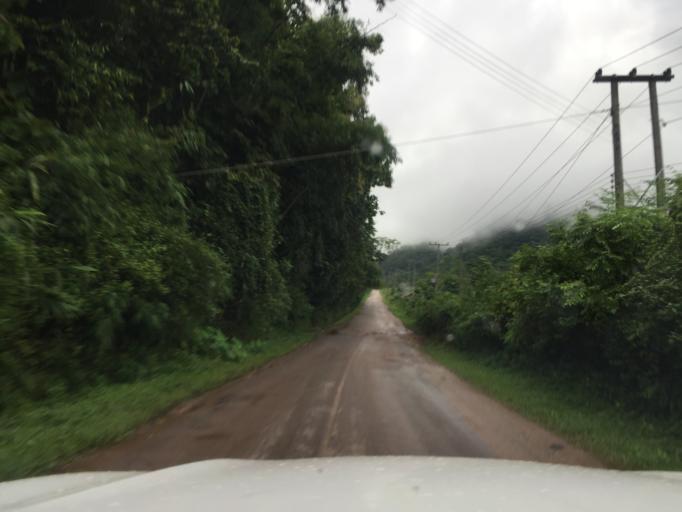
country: LA
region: Oudomxai
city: Muang La
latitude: 20.8363
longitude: 102.1024
